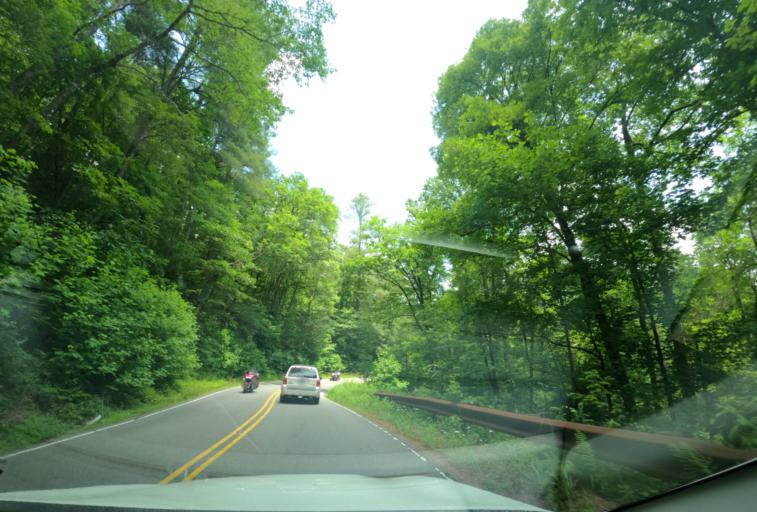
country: US
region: North Carolina
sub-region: Macon County
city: Franklin
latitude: 35.0692
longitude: -83.2359
